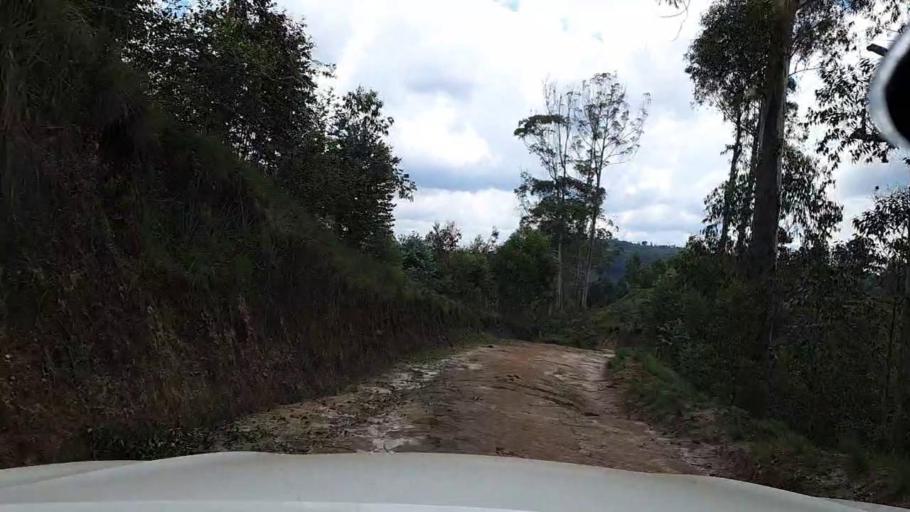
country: RW
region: Southern Province
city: Nzega
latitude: -2.6398
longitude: 29.4794
